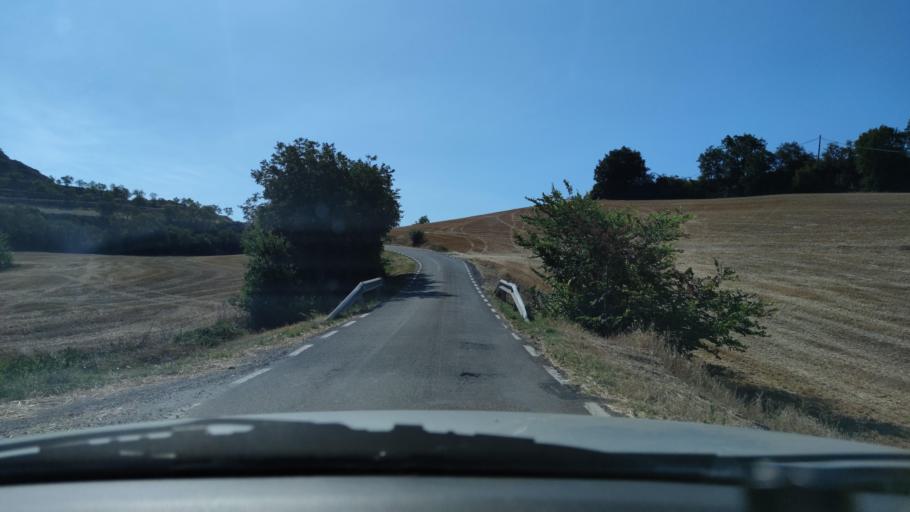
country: ES
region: Catalonia
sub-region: Provincia de Lleida
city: Ivorra
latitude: 41.7369
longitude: 1.3531
